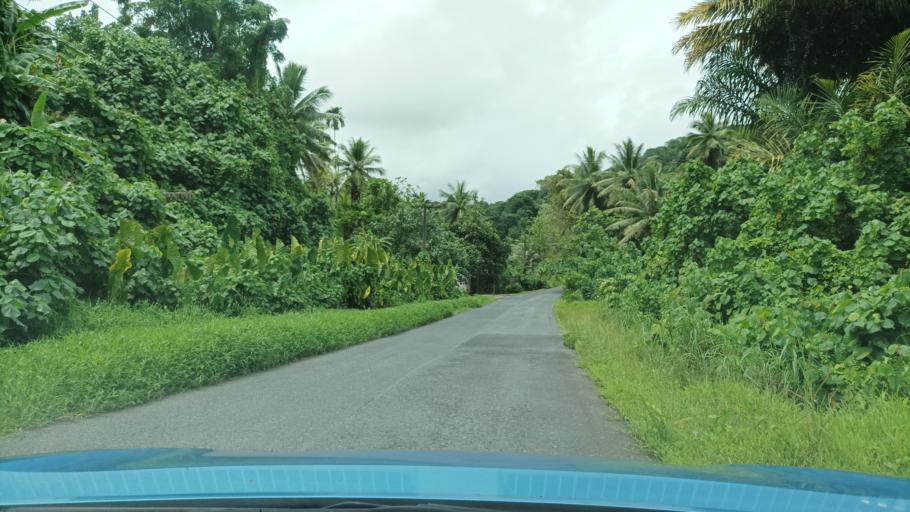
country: FM
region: Pohnpei
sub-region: Madolenihm Municipality
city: Madolenihm Municipality Government
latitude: 6.9193
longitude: 158.3137
